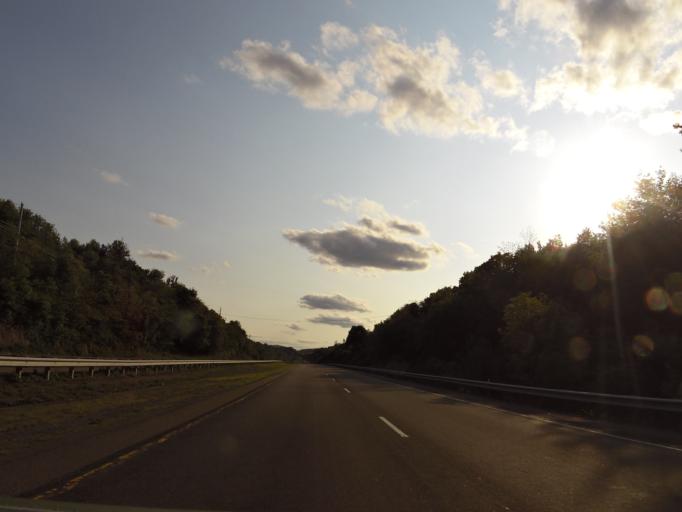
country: US
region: Virginia
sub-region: Tazewell County
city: Claypool Hill
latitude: 37.0059
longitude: -81.8040
